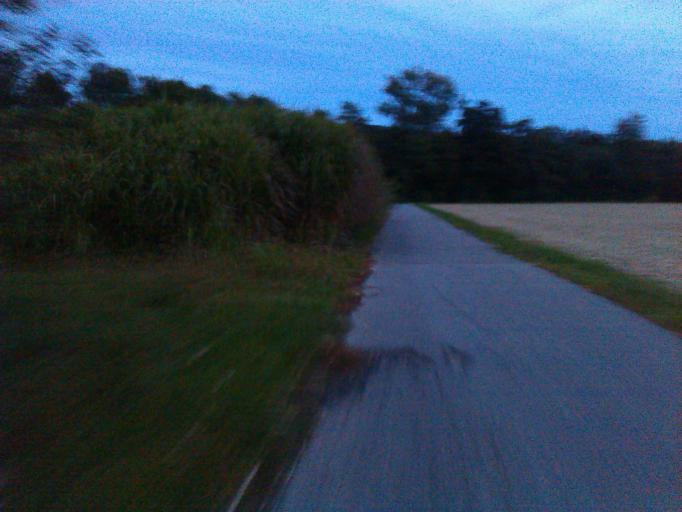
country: DE
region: Baden-Wuerttemberg
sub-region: Karlsruhe Region
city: Sinsheim
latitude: 49.2638
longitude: 8.8454
